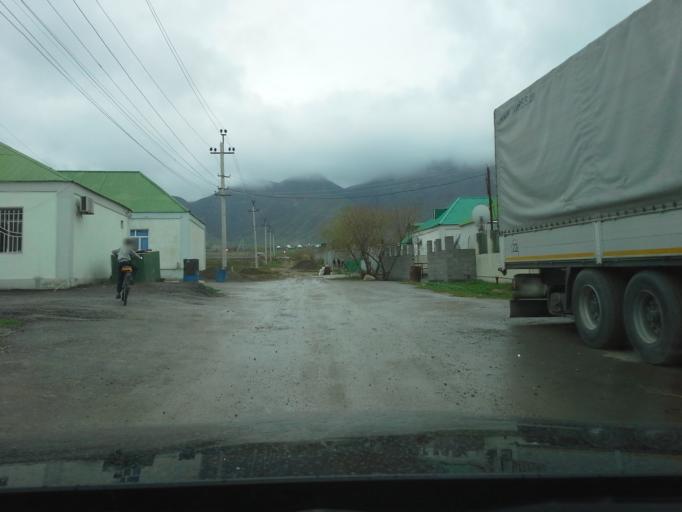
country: TM
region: Ahal
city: Abadan
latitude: 37.9600
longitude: 58.2018
